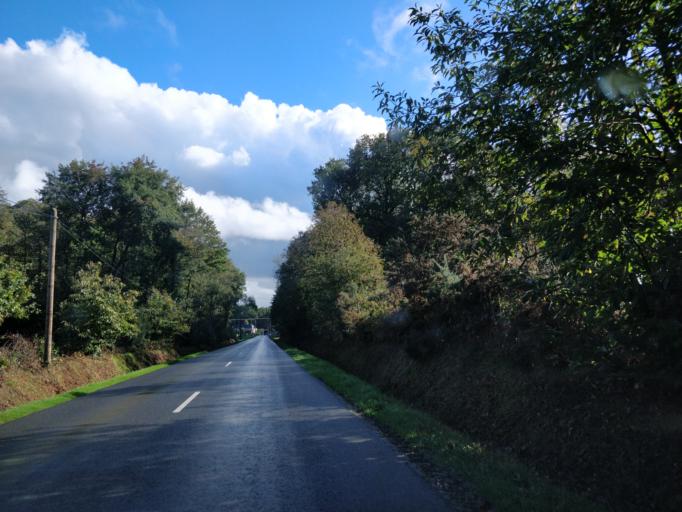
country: FR
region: Brittany
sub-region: Departement d'Ille-et-Vilaine
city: La Bouexiere
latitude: 48.1580
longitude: -1.4135
